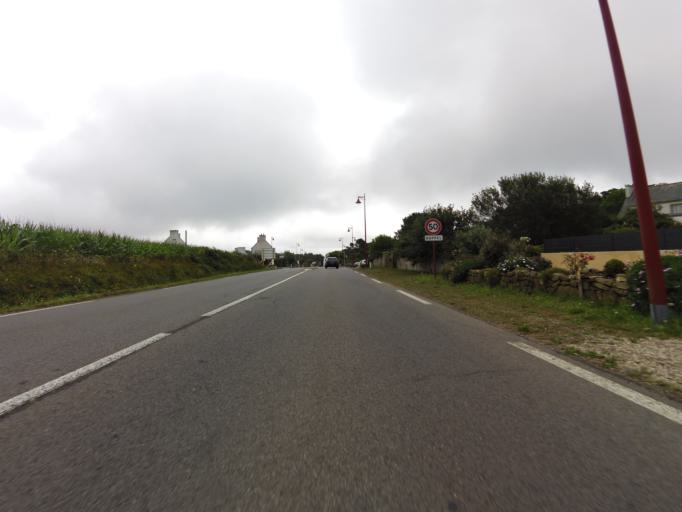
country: FR
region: Brittany
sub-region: Departement du Finistere
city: Plouhinec
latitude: 48.0128
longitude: -4.4784
